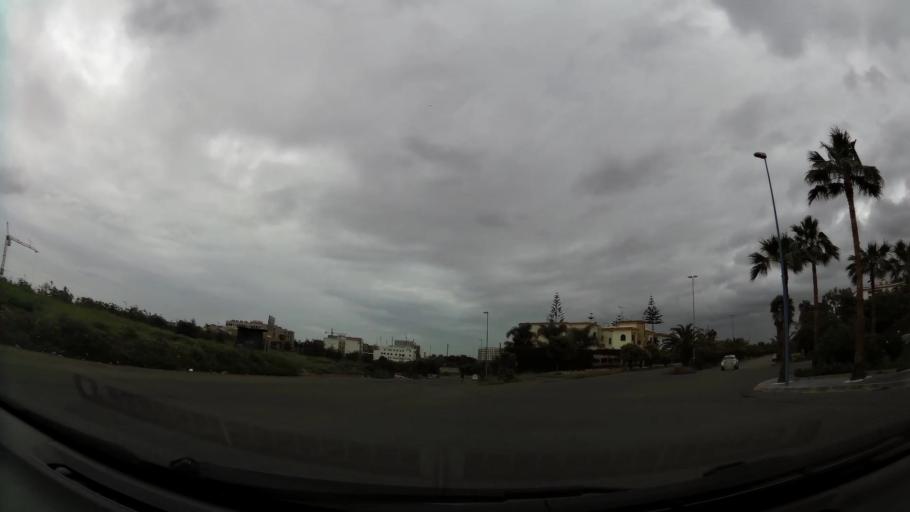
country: MA
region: Grand Casablanca
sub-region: Casablanca
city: Casablanca
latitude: 33.5476
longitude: -7.6361
